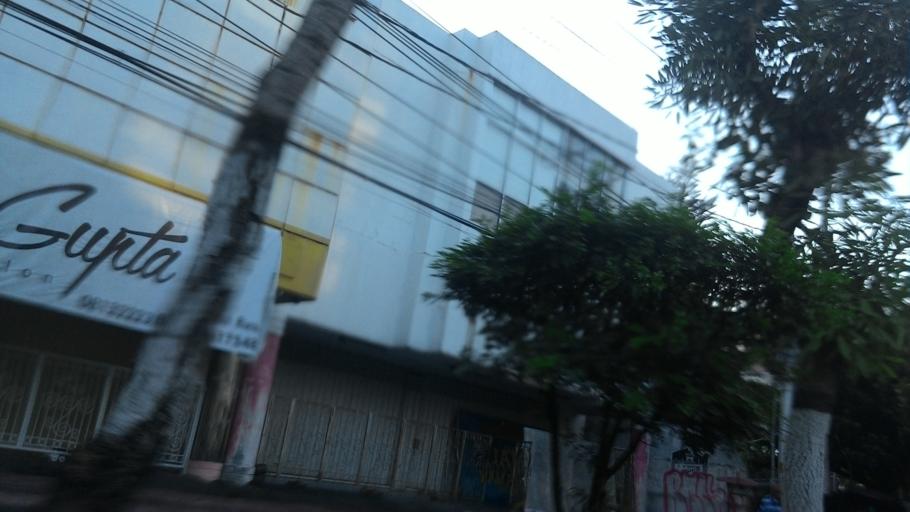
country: ID
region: Daerah Istimewa Yogyakarta
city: Yogyakarta
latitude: -7.7865
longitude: 110.3667
